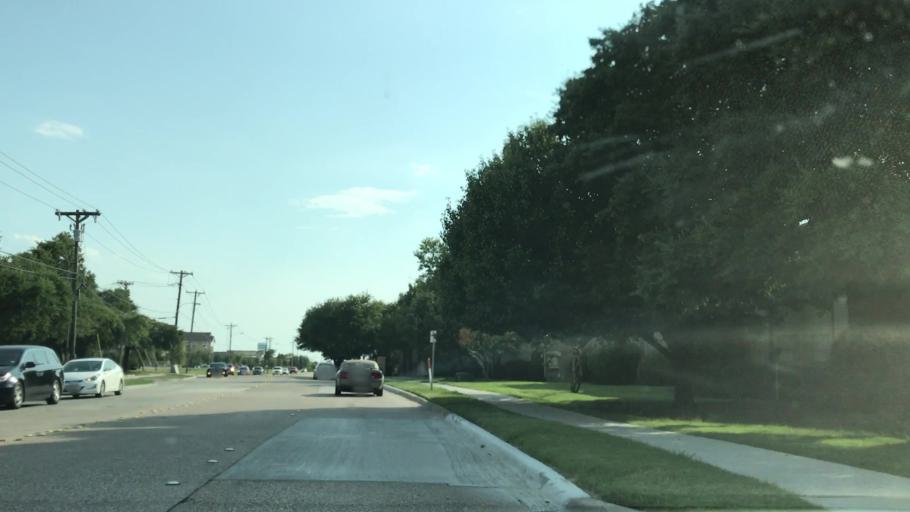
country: US
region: Texas
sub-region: Rockwall County
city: Rockwall
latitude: 32.9122
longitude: -96.4532
